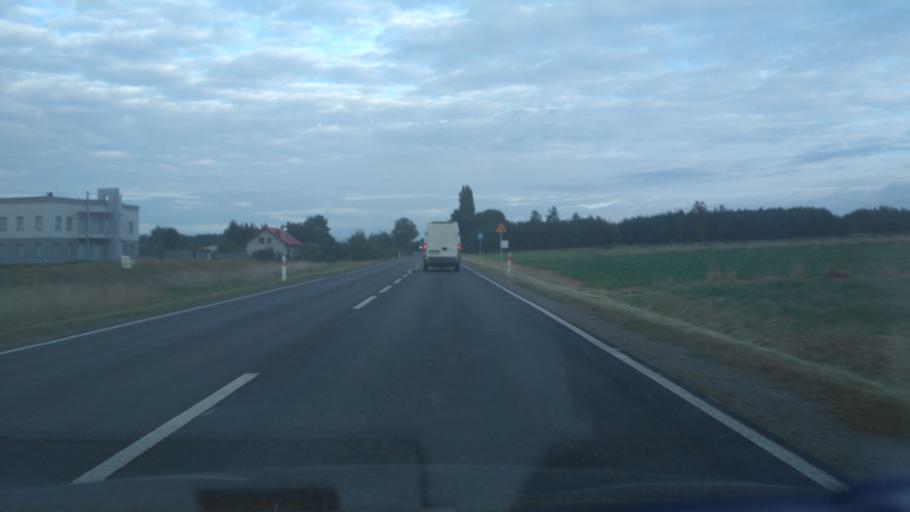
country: PL
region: Lublin Voivodeship
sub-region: Powiat leczynski
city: Spiczyn
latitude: 51.3025
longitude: 22.7421
